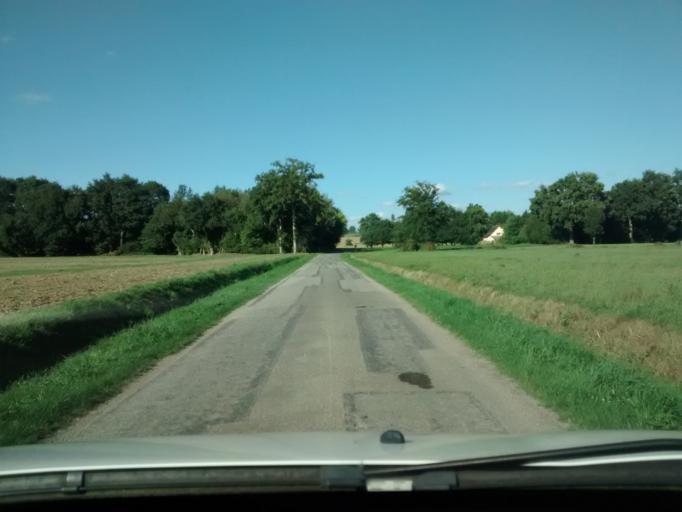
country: FR
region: Brittany
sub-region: Departement d'Ille-et-Vilaine
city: Nouvoitou
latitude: 48.0762
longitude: -1.5624
